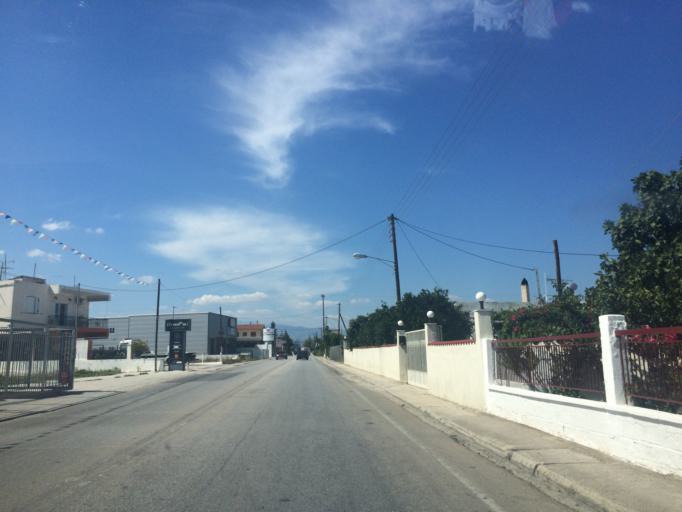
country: GR
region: Peloponnese
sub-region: Nomos Korinthias
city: Lekhaio
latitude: 37.9322
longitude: 22.8577
